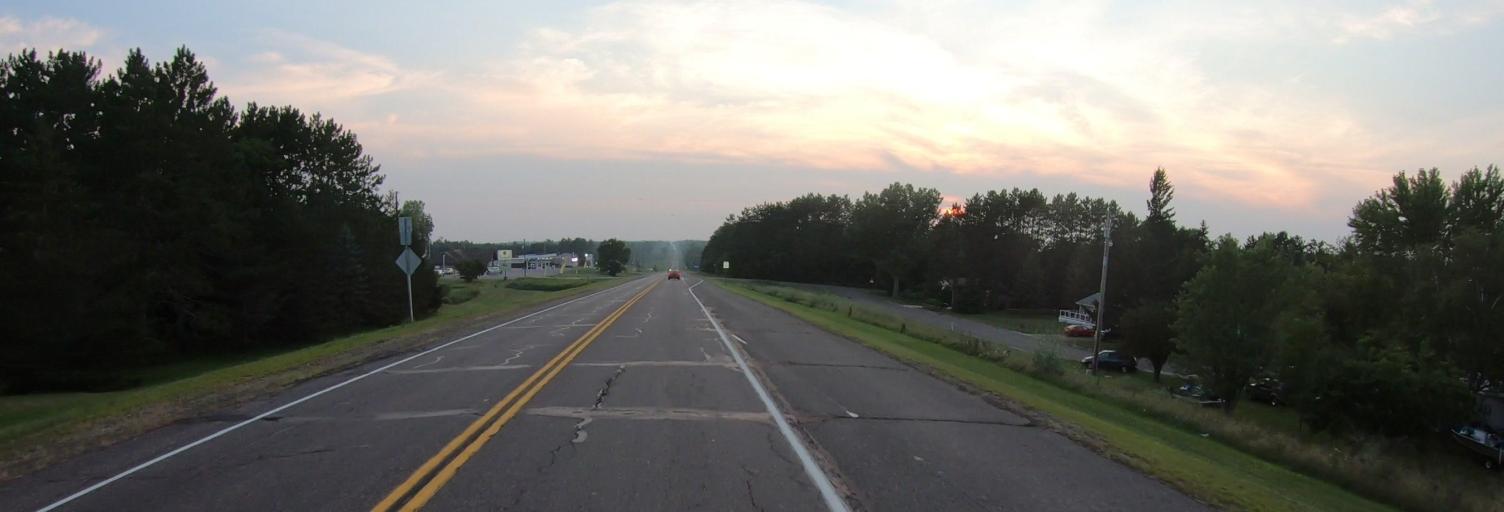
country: US
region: Wisconsin
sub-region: Burnett County
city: Grantsburg
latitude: 45.7730
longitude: -92.6933
